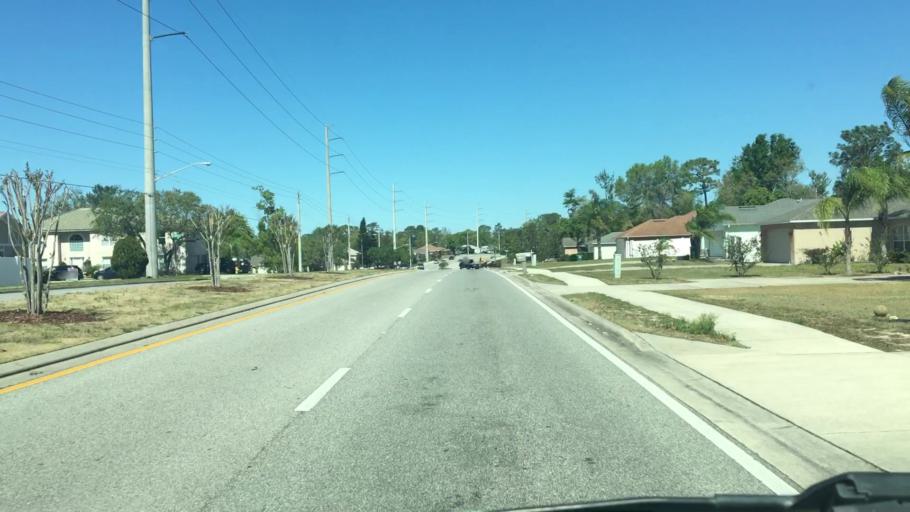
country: US
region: Florida
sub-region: Volusia County
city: Deltona
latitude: 28.9069
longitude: -81.1770
